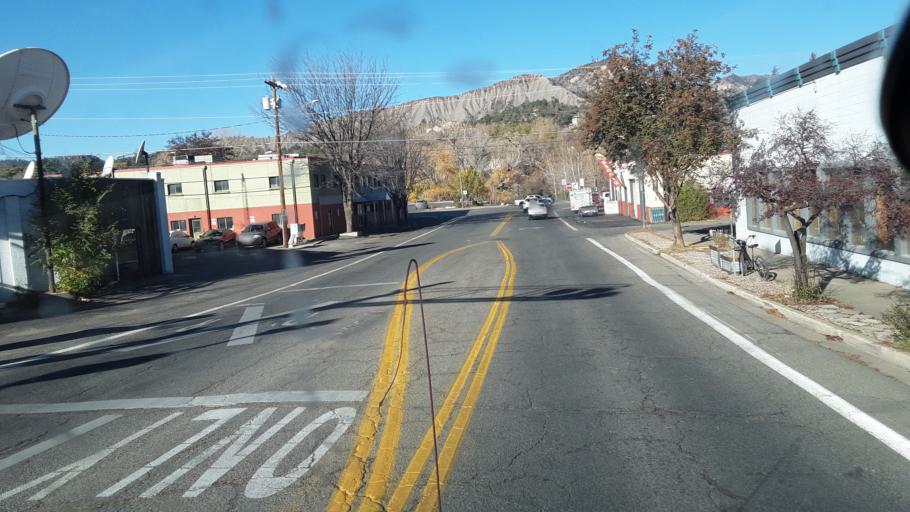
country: US
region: Colorado
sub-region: La Plata County
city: Durango
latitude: 37.2796
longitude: -107.8774
